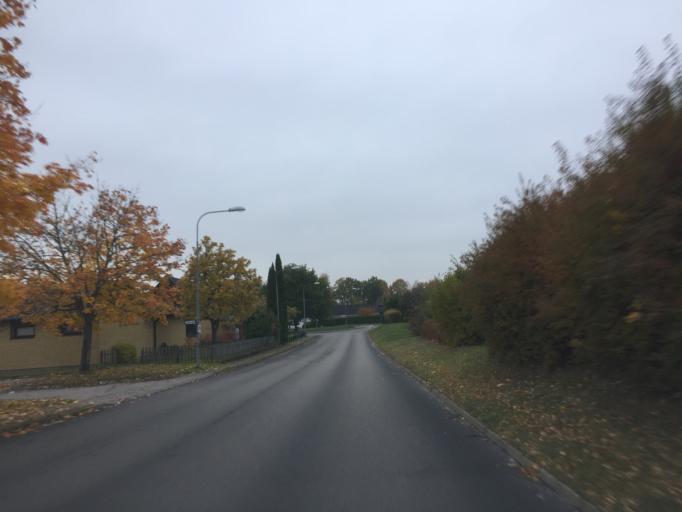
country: SE
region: Vaestra Goetaland
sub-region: Trollhattan
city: Trollhattan
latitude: 58.2779
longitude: 12.3300
